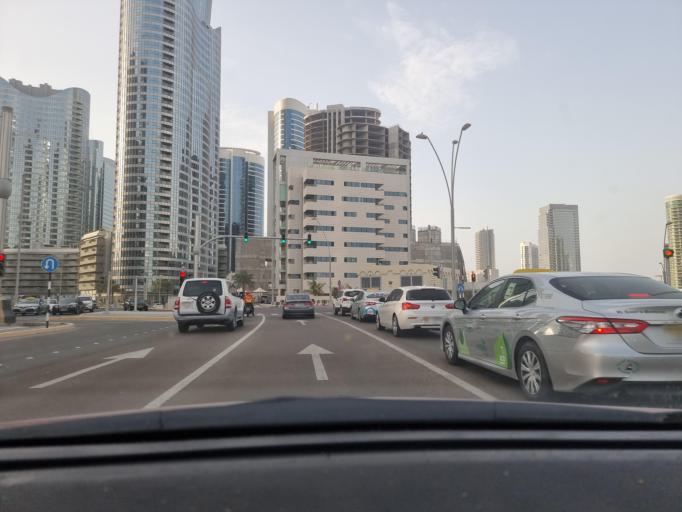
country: AE
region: Abu Dhabi
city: Abu Dhabi
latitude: 24.4963
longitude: 54.4058
